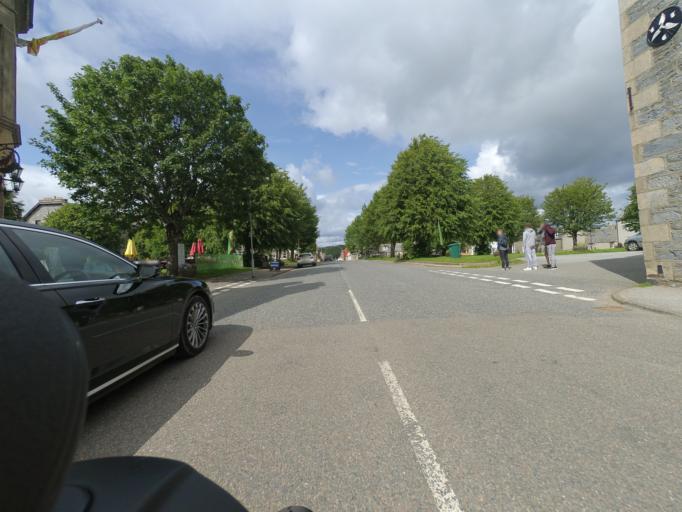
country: GB
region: Scotland
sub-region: Highland
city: Grantown on Spey
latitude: 57.2515
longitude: -3.3790
